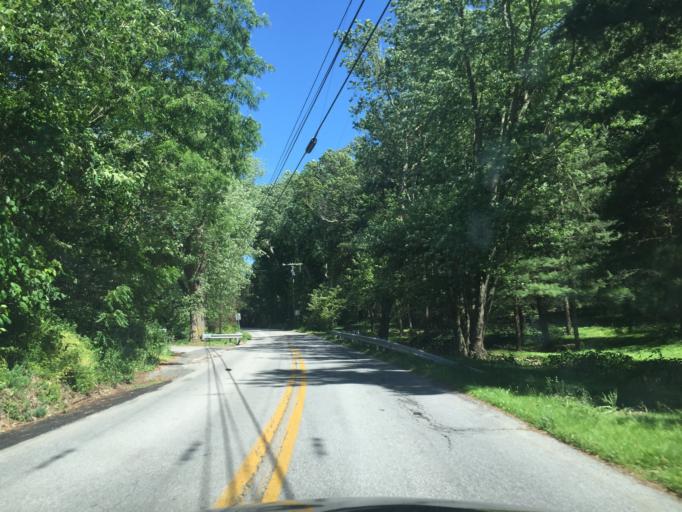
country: US
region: Maryland
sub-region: Carroll County
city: Hampstead
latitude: 39.6165
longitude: -76.8913
